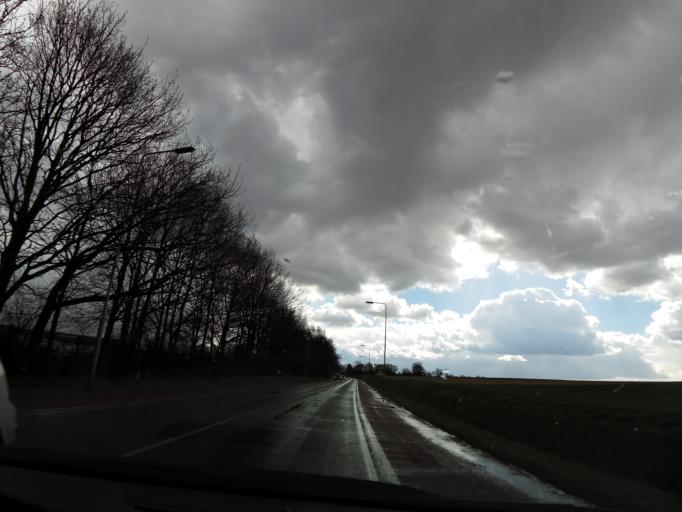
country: NL
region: Limburg
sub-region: Gemeente Sittard-Geleen
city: Limbricht
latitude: 51.0185
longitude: 5.8302
